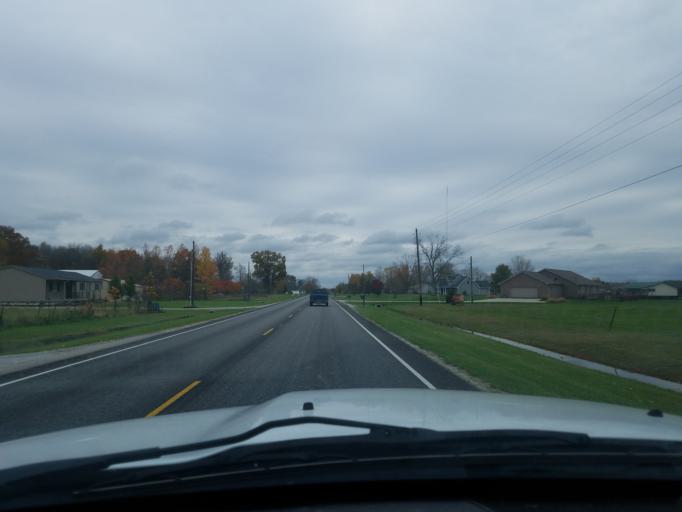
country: US
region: Indiana
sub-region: Jackson County
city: Crothersville
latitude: 38.8515
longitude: -85.8217
